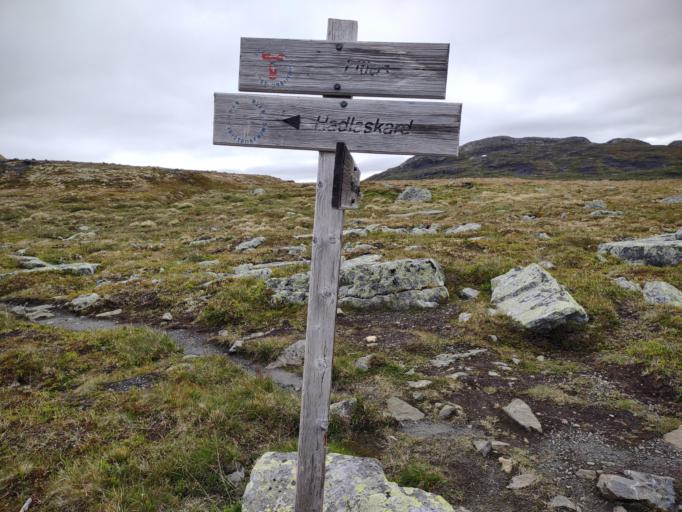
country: NO
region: Hordaland
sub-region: Eidfjord
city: Eidfjord
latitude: 60.1134
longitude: 7.1704
